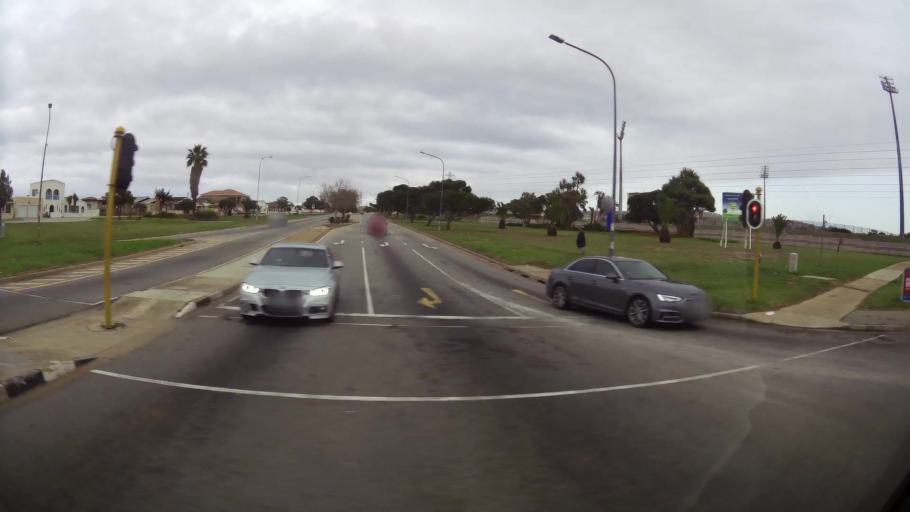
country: ZA
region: Eastern Cape
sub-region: Nelson Mandela Bay Metropolitan Municipality
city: Port Elizabeth
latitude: -33.9148
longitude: 25.5624
